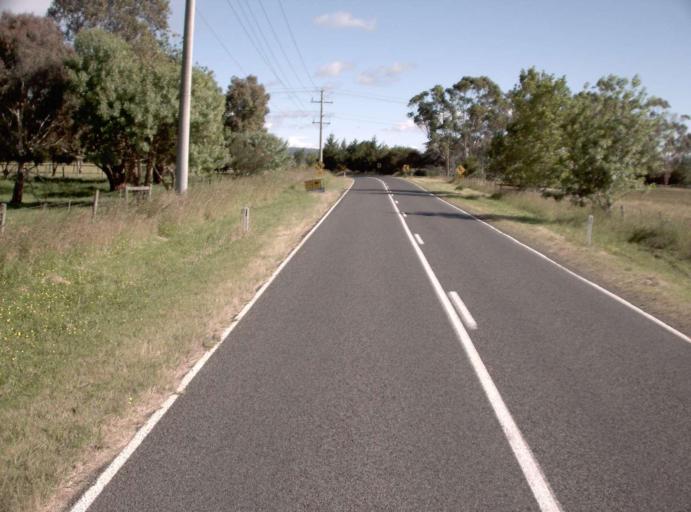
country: AU
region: Victoria
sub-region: Latrobe
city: Traralgon
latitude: -38.1790
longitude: 146.5003
